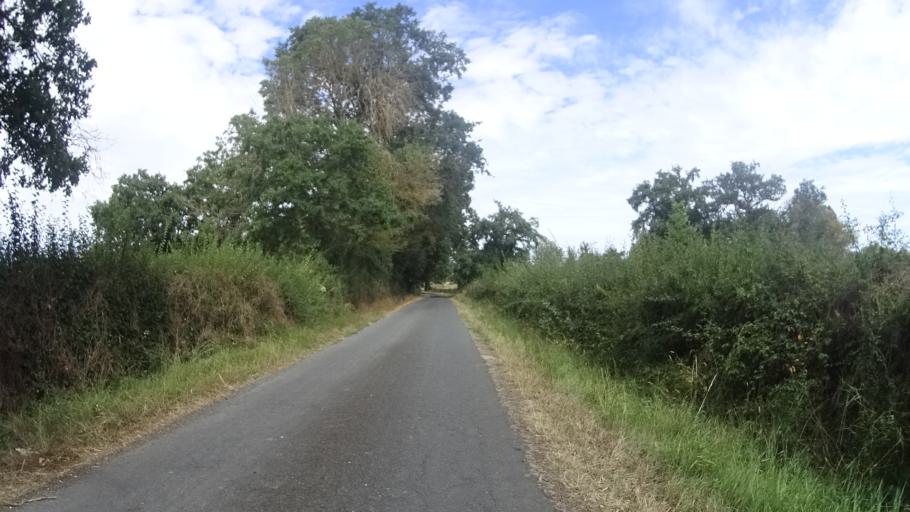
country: FR
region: Auvergne
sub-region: Departement de l'Allier
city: Beaulon
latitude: 46.6490
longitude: 3.6669
